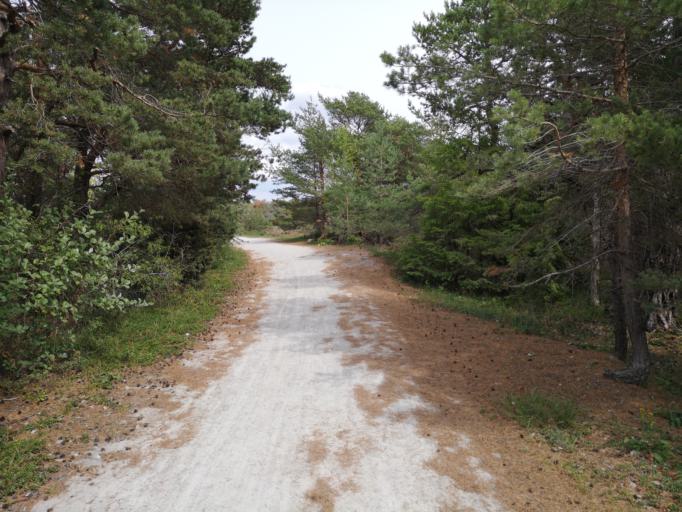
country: SE
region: Gotland
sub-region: Gotland
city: Vibble
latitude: 57.6155
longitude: 18.2595
